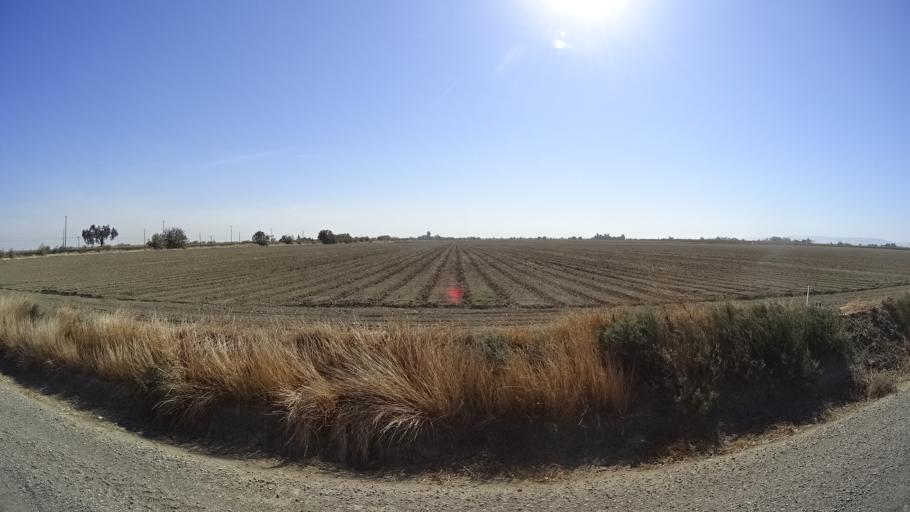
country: US
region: California
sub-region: Yolo County
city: Woodland
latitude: 38.6411
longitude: -121.7679
